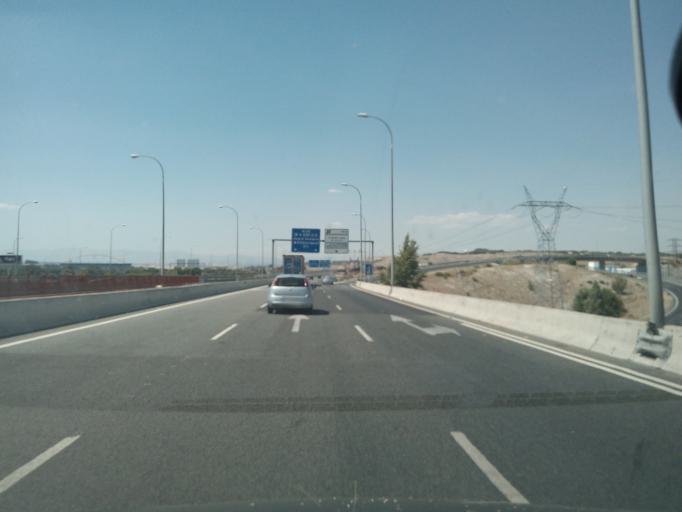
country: ES
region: Madrid
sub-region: Provincia de Madrid
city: San Fernando de Henares
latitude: 40.4473
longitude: -3.5164
